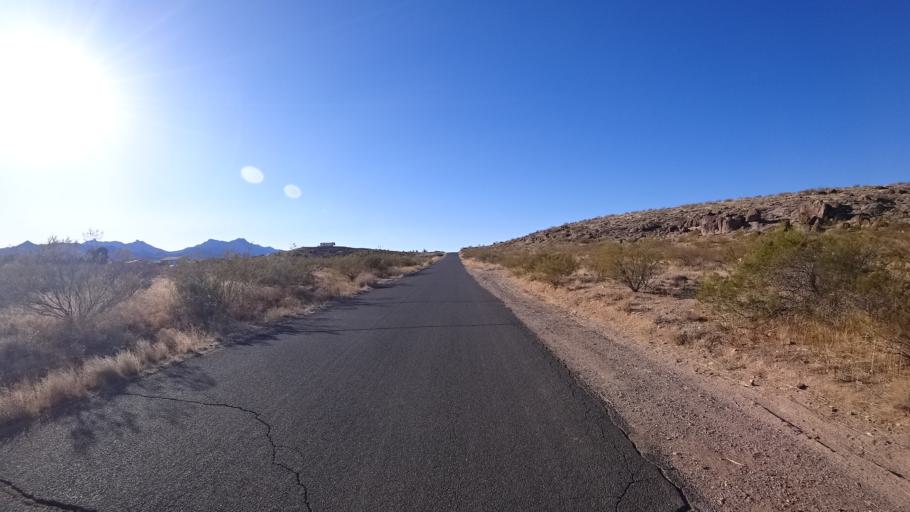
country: US
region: Arizona
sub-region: Mohave County
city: Kingman
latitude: 35.2078
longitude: -114.0026
